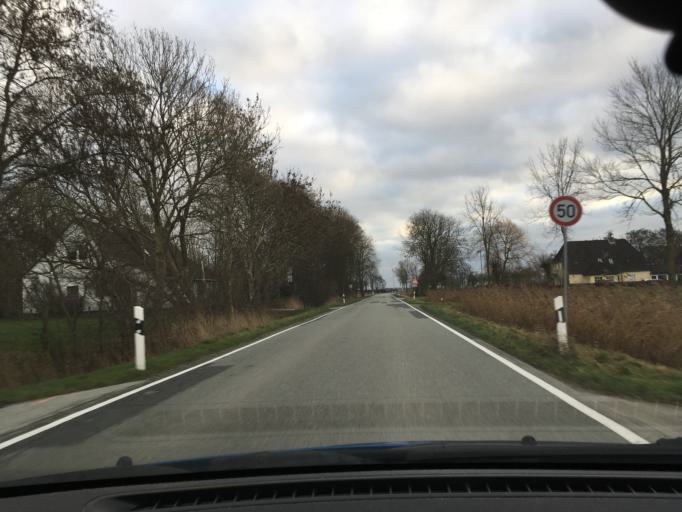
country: DE
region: Schleswig-Holstein
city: Norderwohrden
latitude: 54.1960
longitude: 9.0338
